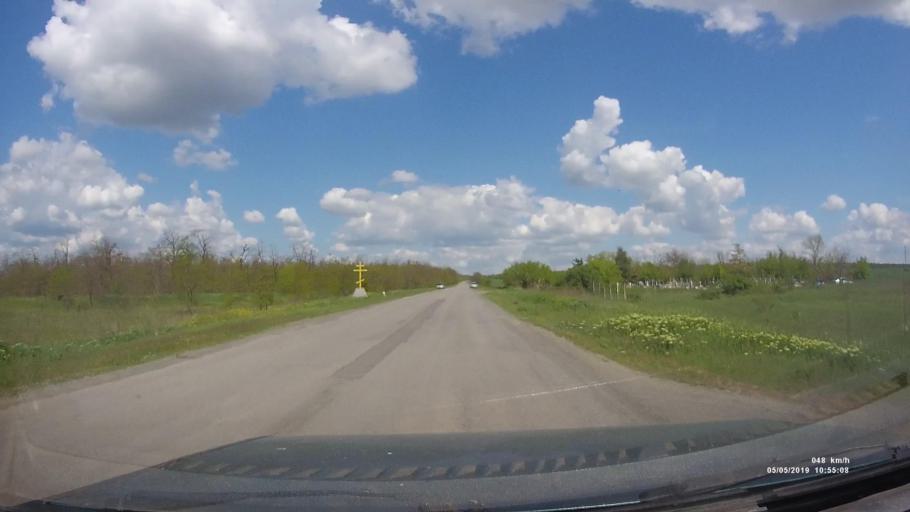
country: RU
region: Rostov
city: Ust'-Donetskiy
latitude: 47.6631
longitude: 40.8217
